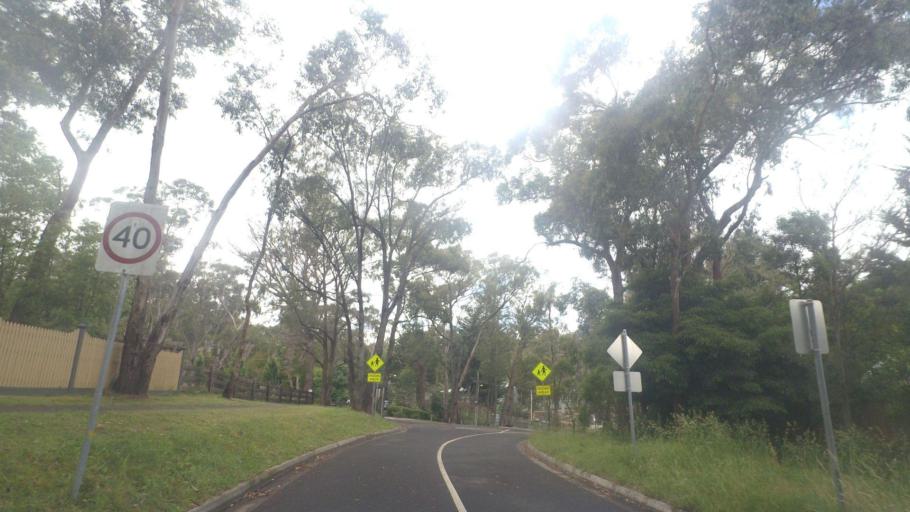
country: AU
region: Victoria
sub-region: Yarra Ranges
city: Mount Evelyn
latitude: -37.7783
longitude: 145.3680
